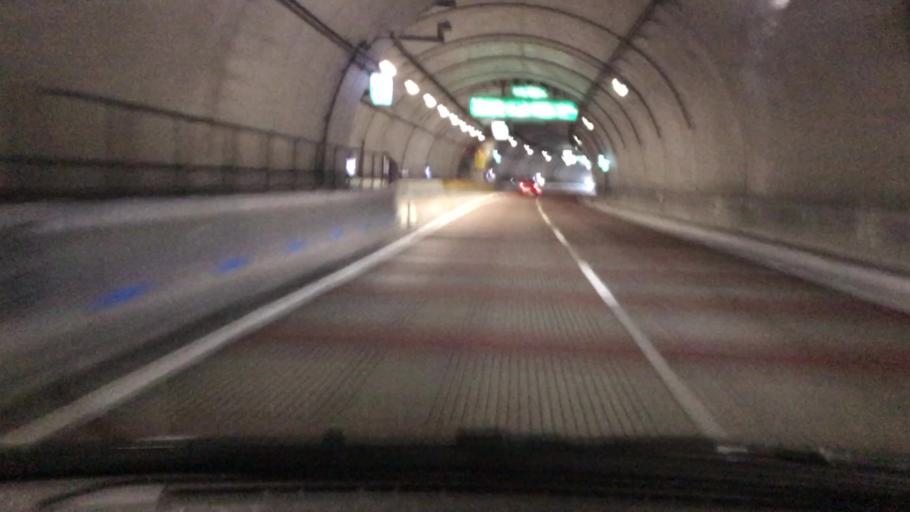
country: JP
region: Hyogo
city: Sandacho
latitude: 34.8274
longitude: 135.2580
